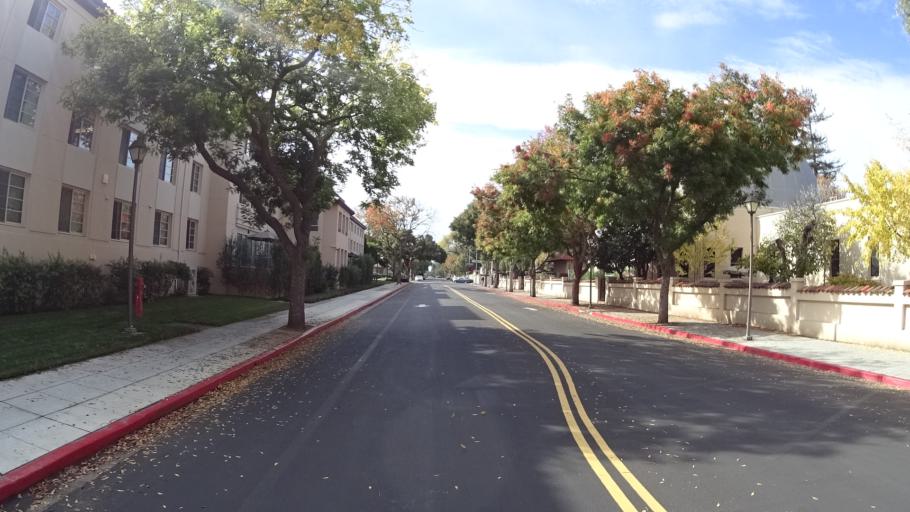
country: US
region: California
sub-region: Santa Clara County
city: Santa Clara
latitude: 37.3478
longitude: -121.9406
